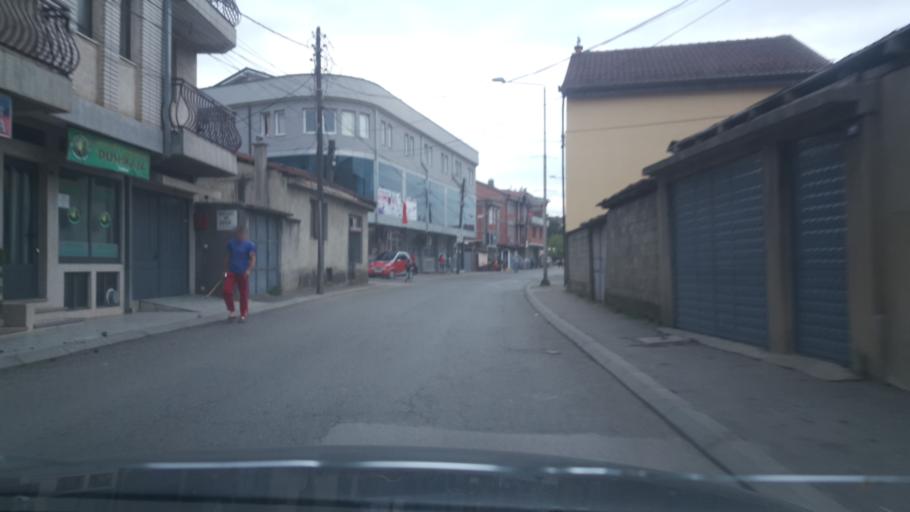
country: XK
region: Gjakova
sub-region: Komuna e Gjakoves
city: Gjakove
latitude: 42.3881
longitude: 20.4298
